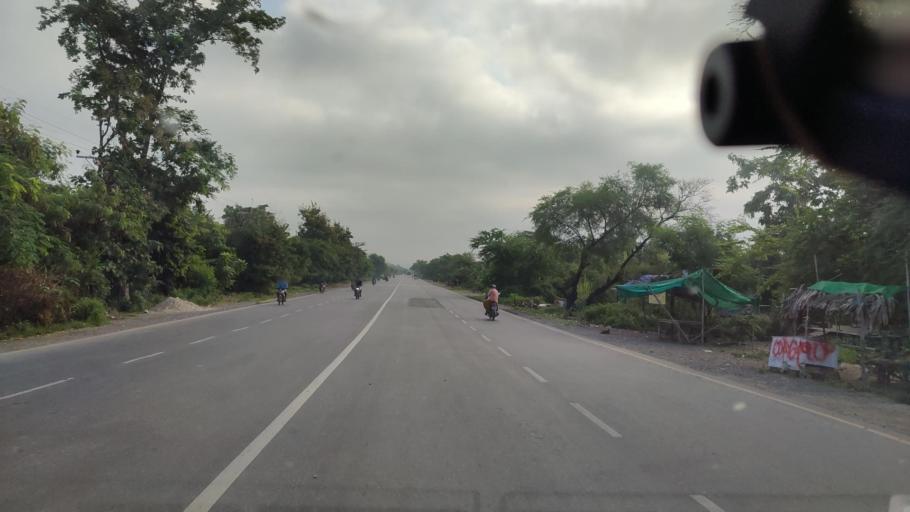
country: MM
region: Mandalay
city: Mandalay
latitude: 22.0705
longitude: 96.1363
